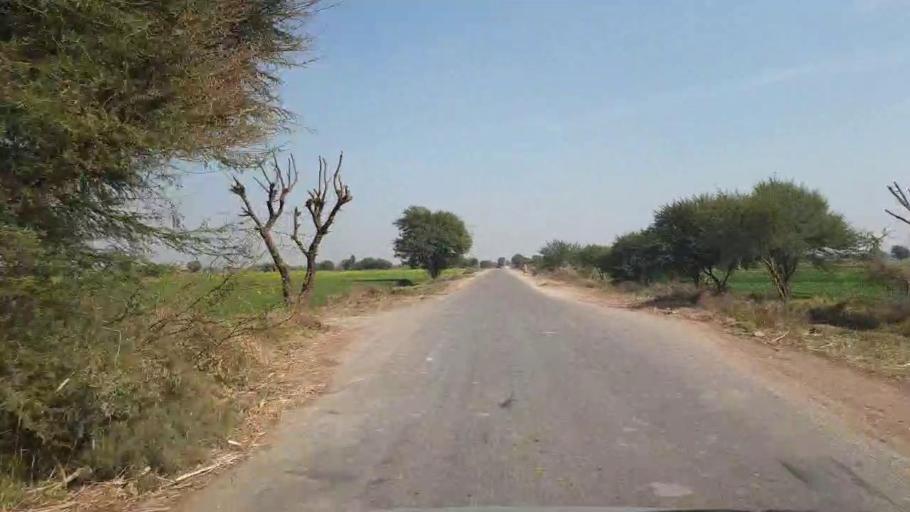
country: PK
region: Sindh
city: Chambar
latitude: 25.3117
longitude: 68.8134
